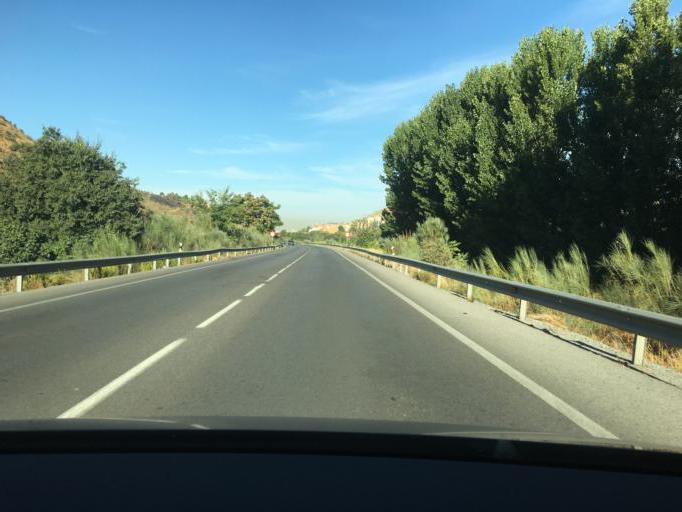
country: ES
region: Andalusia
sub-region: Provincia de Granada
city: Huetor Vega
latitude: 37.1603
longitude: -3.5595
